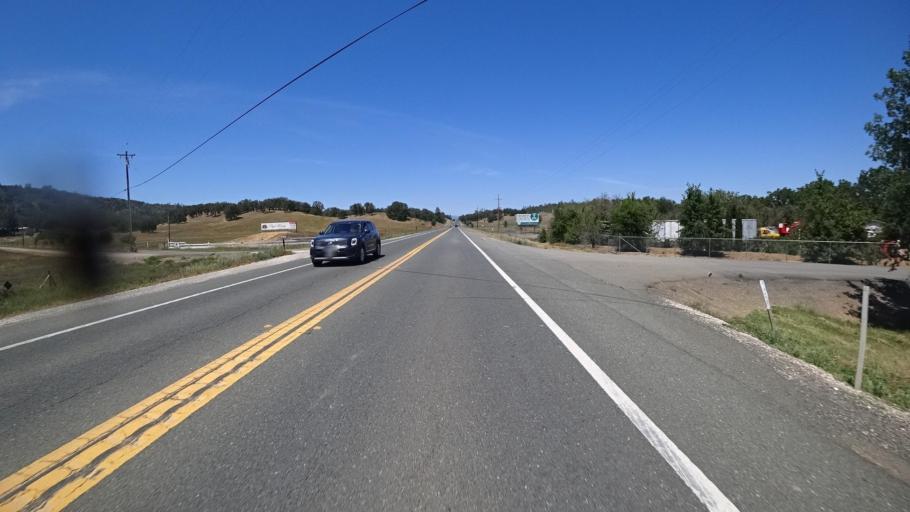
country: US
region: California
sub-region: Lake County
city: Lower Lake
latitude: 38.8919
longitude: -122.6059
